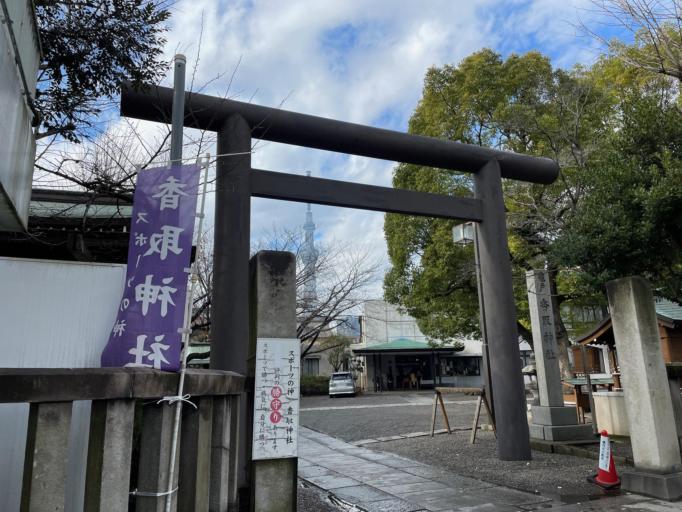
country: JP
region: Tokyo
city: Urayasu
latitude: 35.7039
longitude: 139.8256
